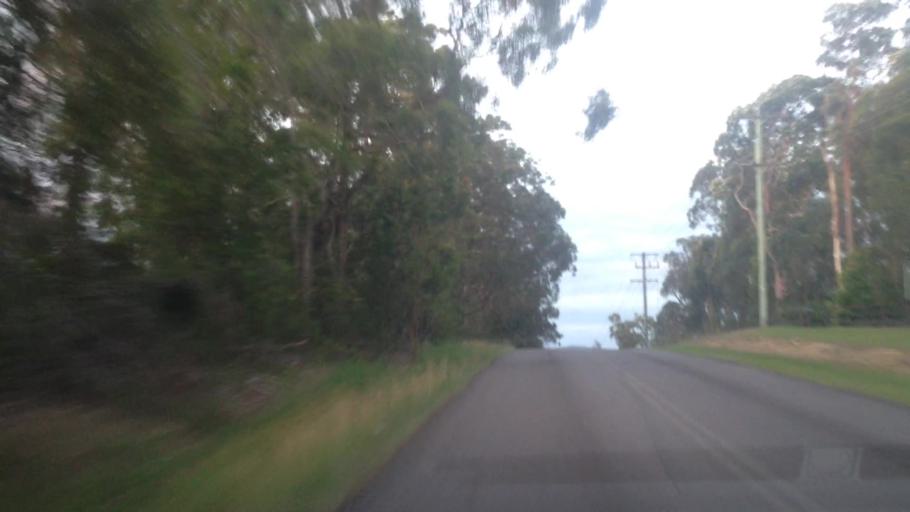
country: AU
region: New South Wales
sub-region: Lake Macquarie Shire
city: Cooranbong
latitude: -33.0759
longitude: 151.4736
